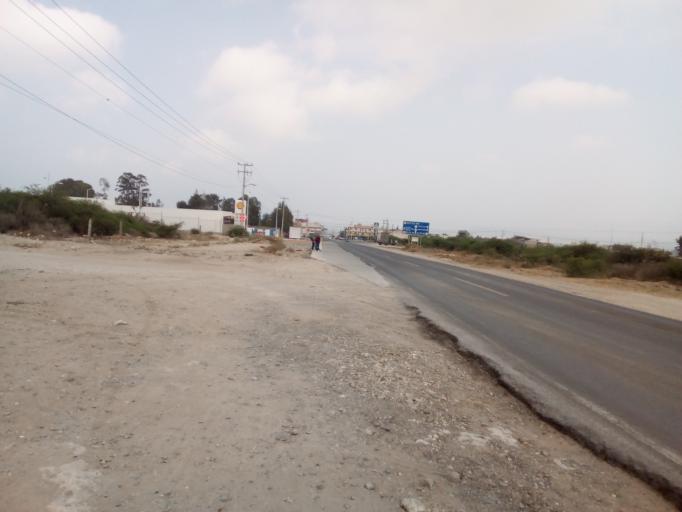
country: MX
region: Guerrero
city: San Luis de la Paz
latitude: 21.2866
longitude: -100.5075
